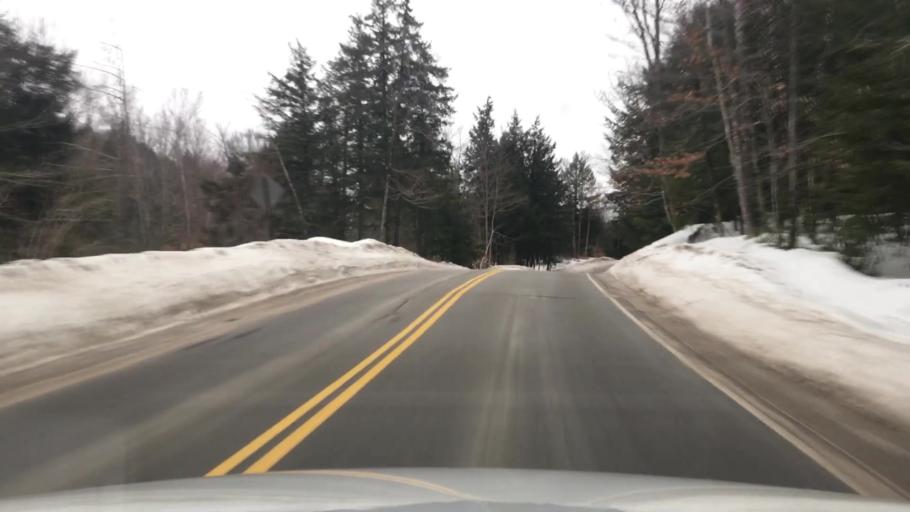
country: US
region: Maine
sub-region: Oxford County
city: Hiram
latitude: 43.9013
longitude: -70.7979
